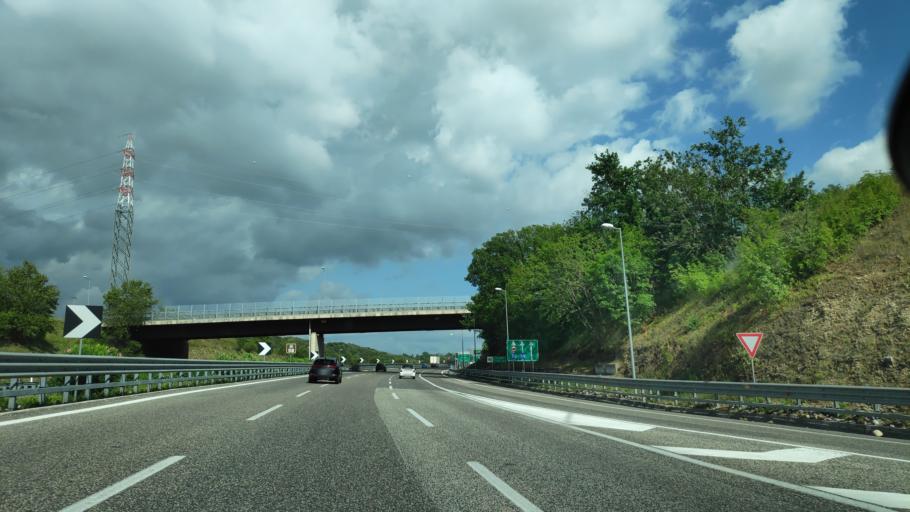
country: IT
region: Campania
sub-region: Provincia di Salerno
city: Contursi Terme
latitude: 40.6284
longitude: 15.2311
